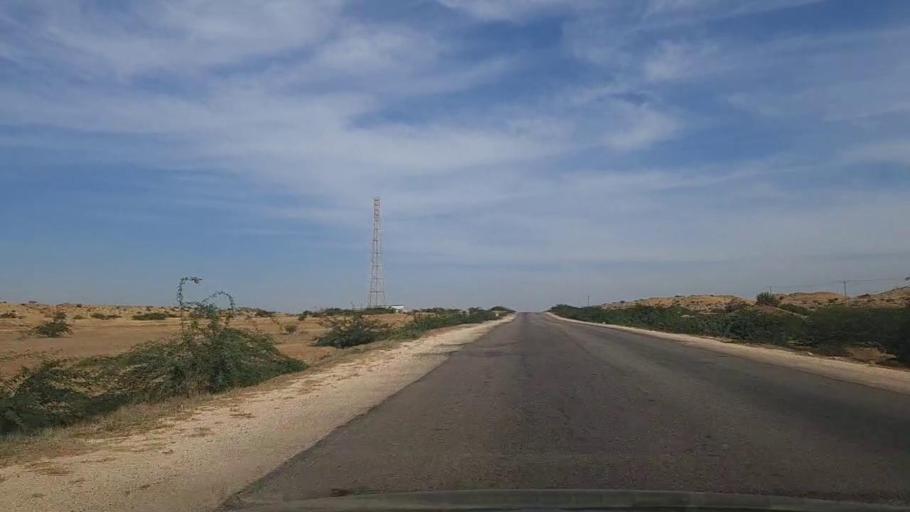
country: PK
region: Sindh
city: Daro Mehar
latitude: 25.0032
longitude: 68.1706
